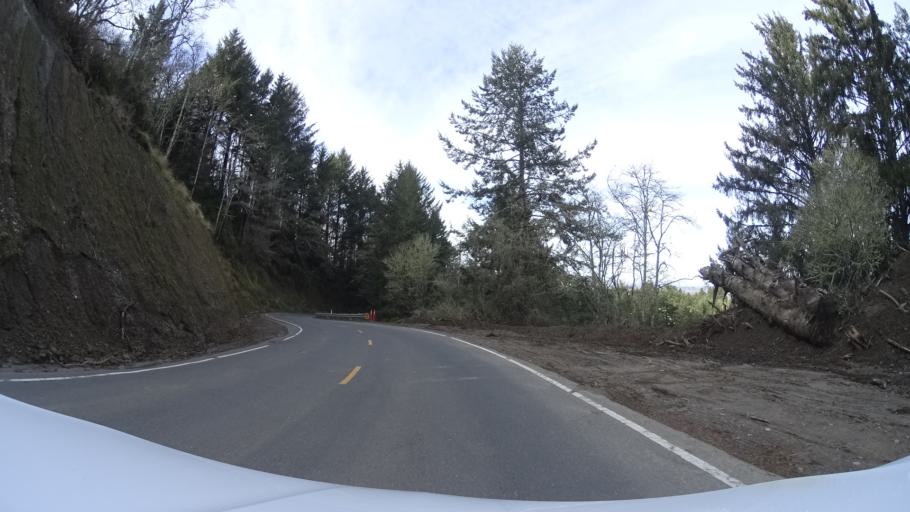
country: US
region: California
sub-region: Humboldt County
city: Ferndale
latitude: 40.5618
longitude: -124.2730
